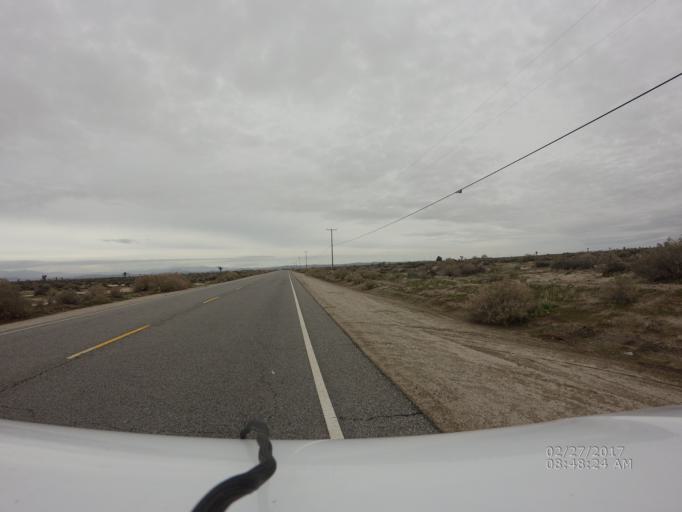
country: US
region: California
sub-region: Los Angeles County
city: Lancaster
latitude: 34.7291
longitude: -118.0770
